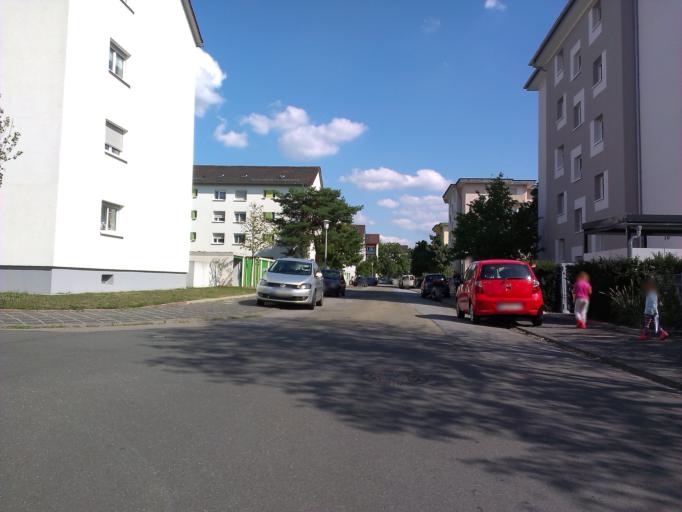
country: DE
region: Baden-Wuerttemberg
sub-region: Karlsruhe Region
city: Mannheim
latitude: 49.5453
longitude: 8.4756
